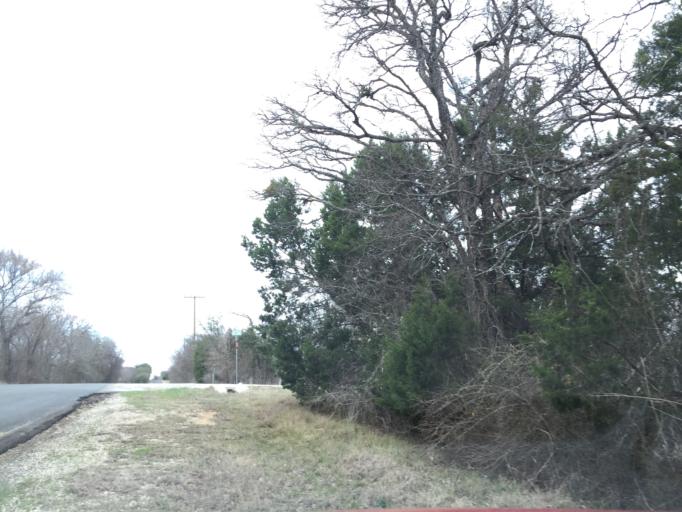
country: US
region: Texas
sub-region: Burnet County
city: Bertram
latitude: 30.7377
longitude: -97.9366
